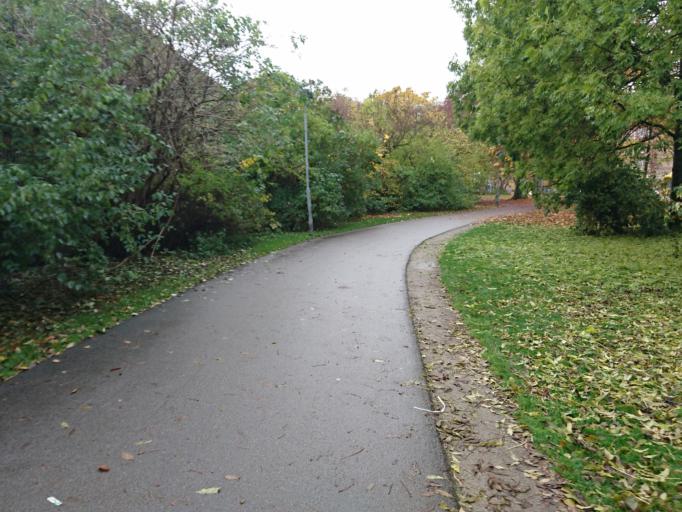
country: SE
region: Skane
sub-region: Lunds Kommun
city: Lund
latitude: 55.6959
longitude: 13.1918
